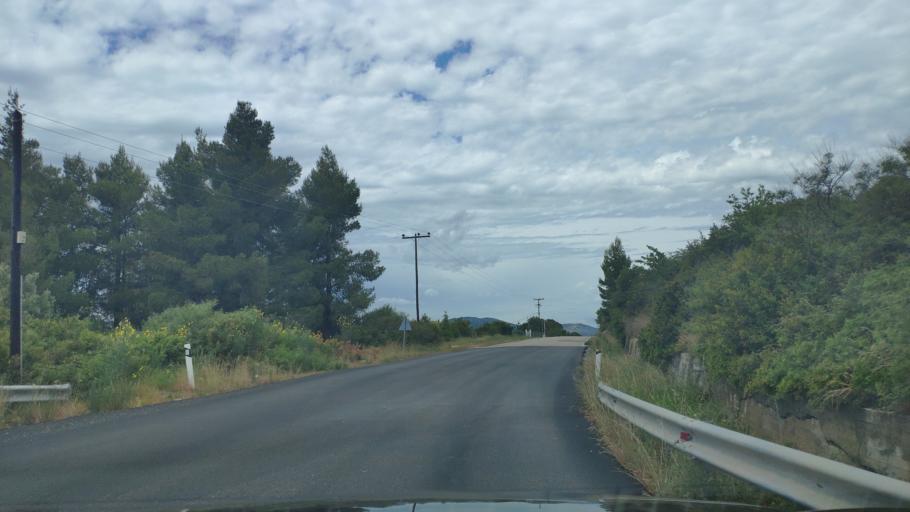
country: GR
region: West Greece
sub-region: Nomos Aitolias kai Akarnanias
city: Palairos
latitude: 38.7587
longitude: 20.8843
